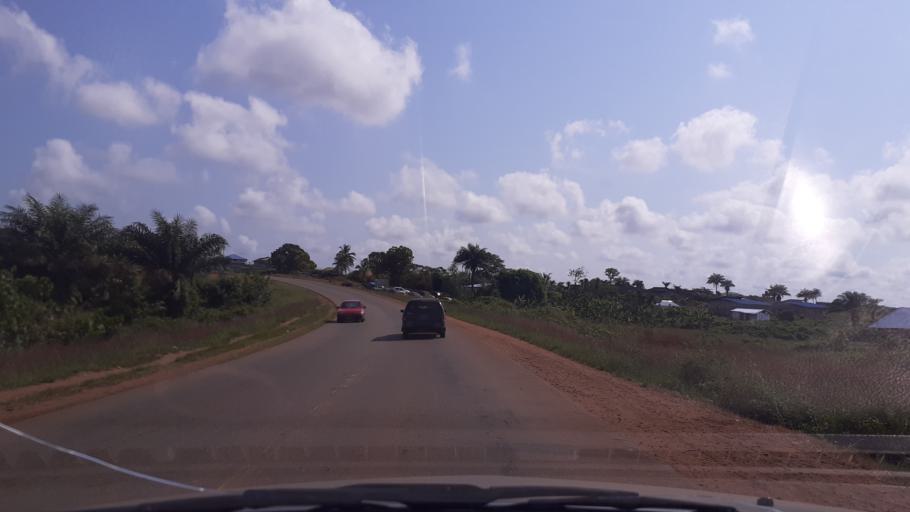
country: LR
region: Montserrado
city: Bensonville City
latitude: 6.2228
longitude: -10.5378
